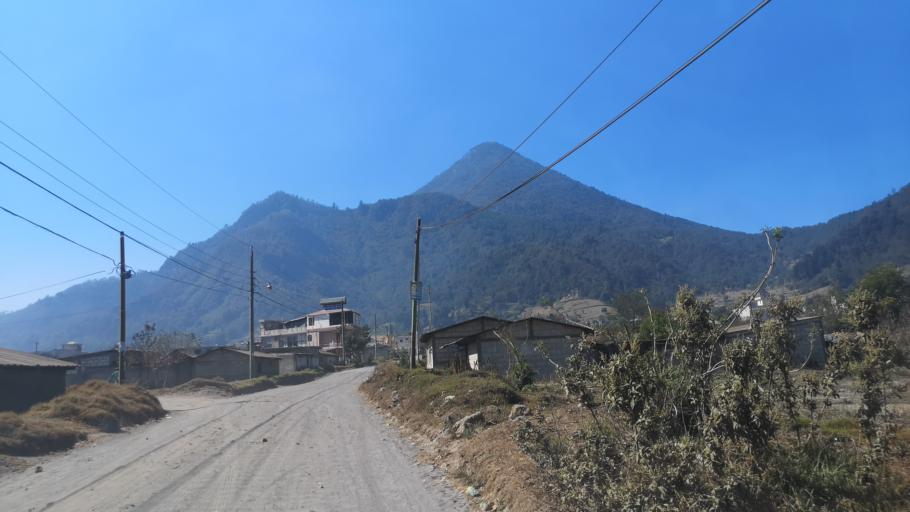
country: GT
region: Quetzaltenango
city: Quetzaltenango
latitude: 14.7932
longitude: -91.5436
